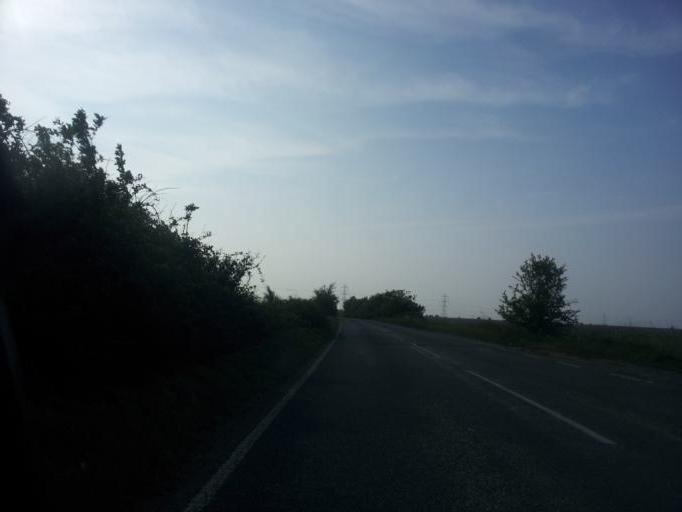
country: GB
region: England
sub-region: Kent
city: Queenborough
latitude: 51.3896
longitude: 0.7400
